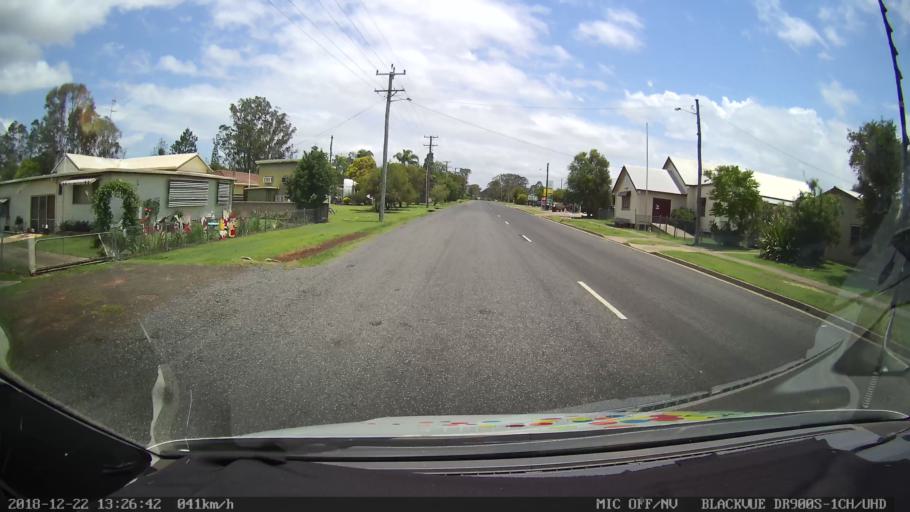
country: AU
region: New South Wales
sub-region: Clarence Valley
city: Coutts Crossing
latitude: -29.8274
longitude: 152.8918
